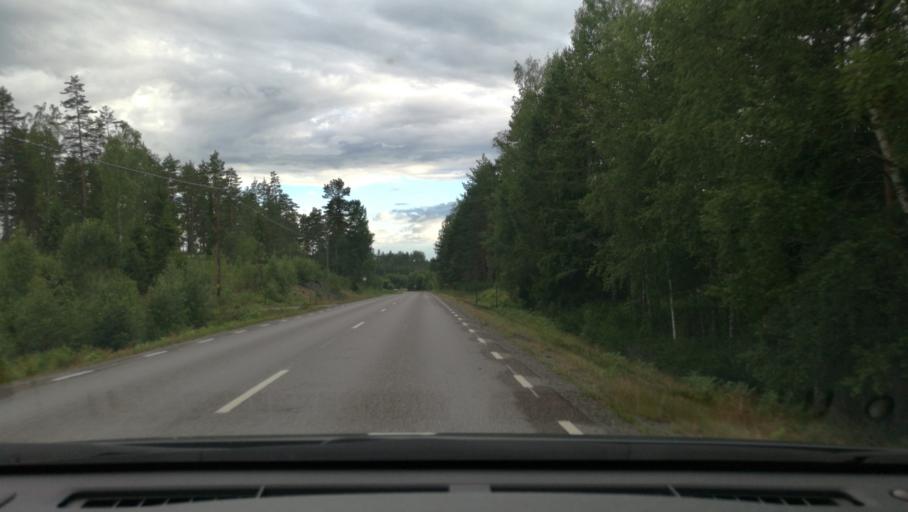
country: SE
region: OEstergoetland
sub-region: Norrkopings Kommun
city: Svartinge
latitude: 58.7276
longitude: 15.9474
